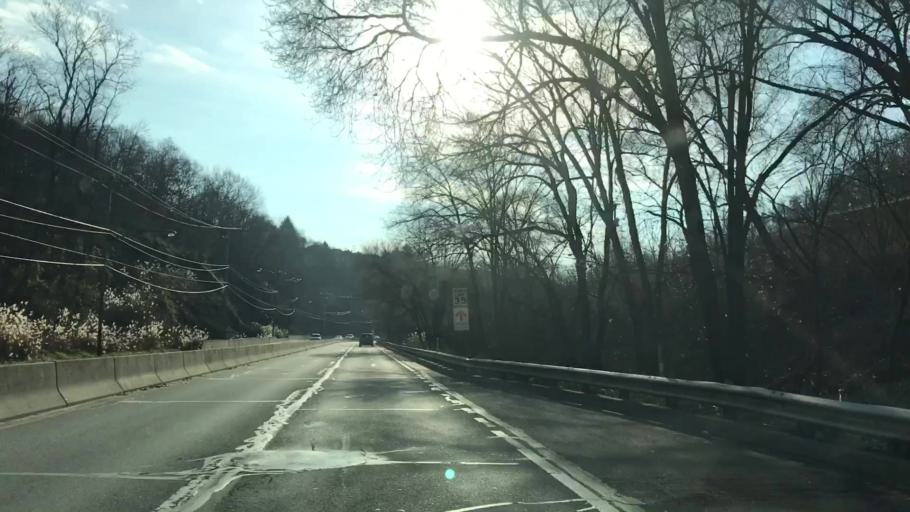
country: US
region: Pennsylvania
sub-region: Allegheny County
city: Pittsburgh
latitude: 40.4233
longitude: -80.0172
